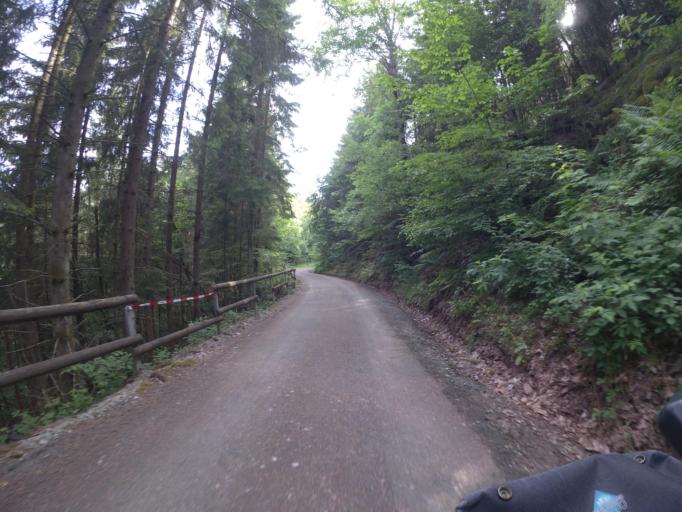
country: DE
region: Saarland
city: Nonnweiler
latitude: 49.6224
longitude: 6.9380
